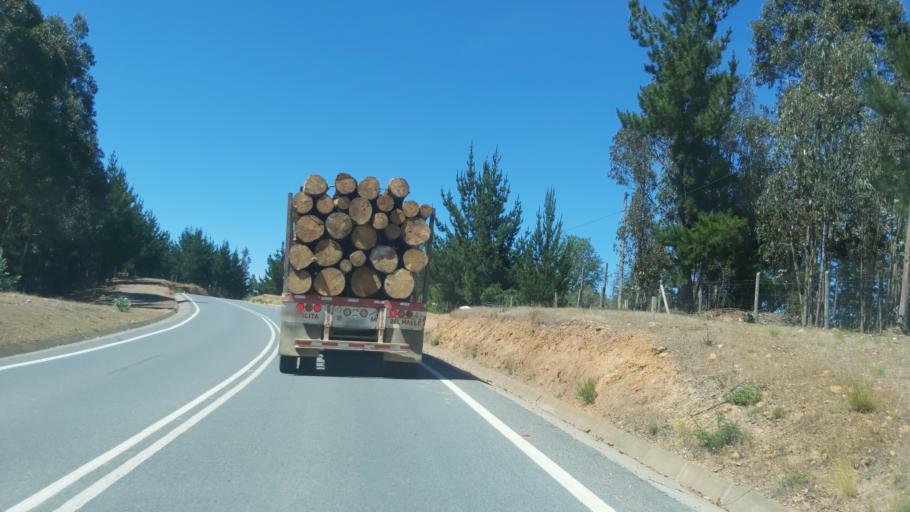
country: CL
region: Maule
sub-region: Provincia de Talca
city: Constitucion
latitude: -34.9281
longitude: -71.9873
